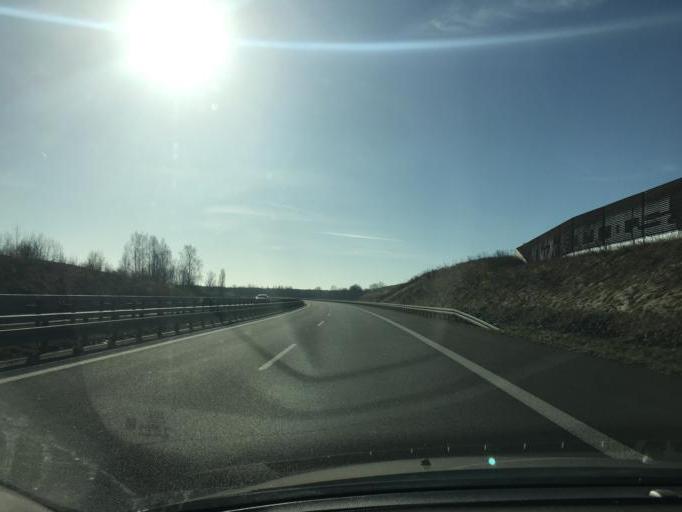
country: DE
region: Saxony
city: Frohburg
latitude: 51.0804
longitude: 12.5425
